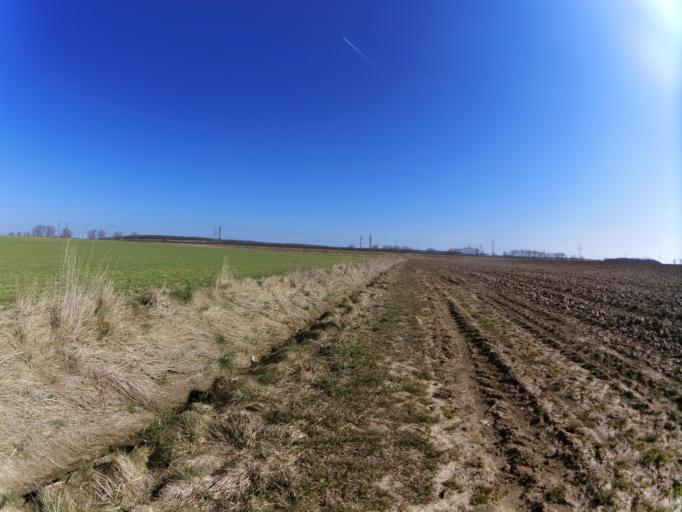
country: DE
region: Bavaria
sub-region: Regierungsbezirk Unterfranken
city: Bergtheim
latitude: 49.8915
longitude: 10.0789
